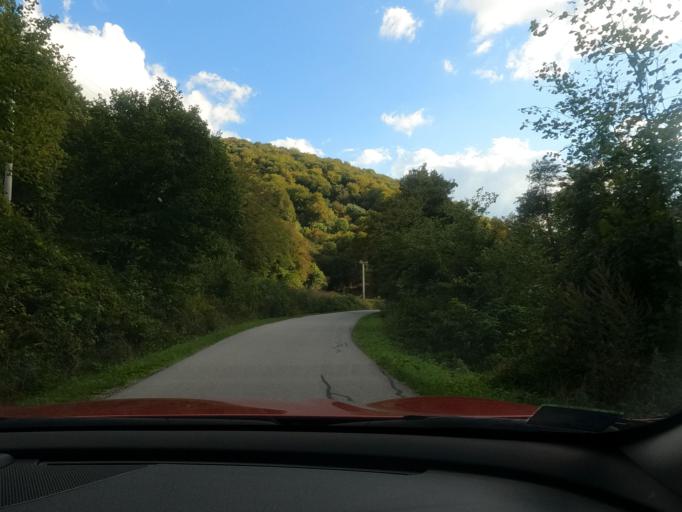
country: HR
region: Sisacko-Moslavacka
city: Petrinja
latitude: 45.4029
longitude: 16.2468
